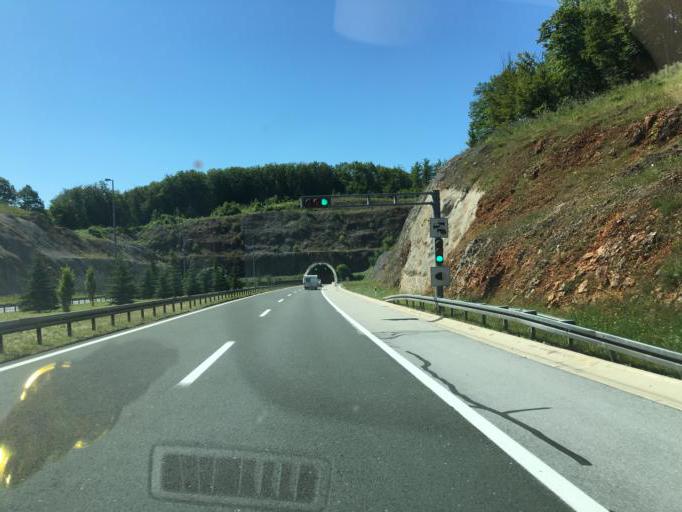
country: HR
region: Licko-Senjska
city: Otocac
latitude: 44.8759
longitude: 15.2059
